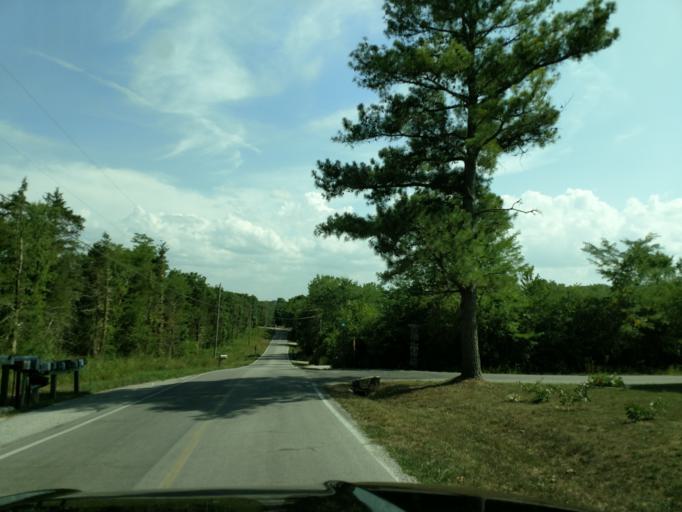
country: US
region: Missouri
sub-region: Barry County
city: Shell Knob
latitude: 36.6018
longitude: -93.5814
